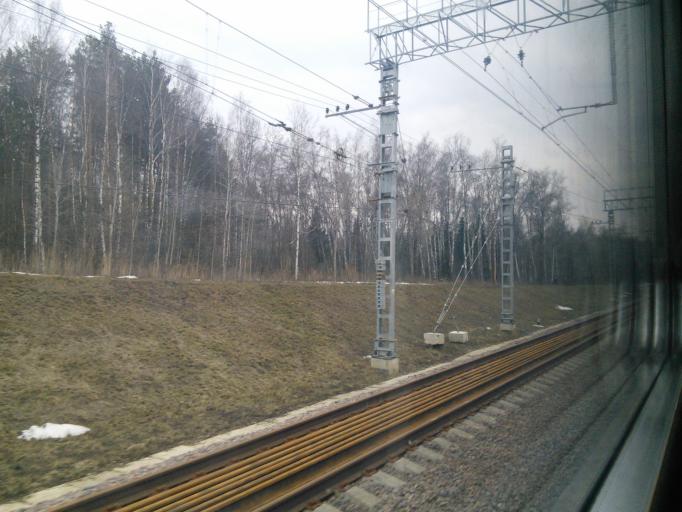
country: RU
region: Moskovskaya
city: Vostryakovo
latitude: 55.4322
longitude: 37.8497
